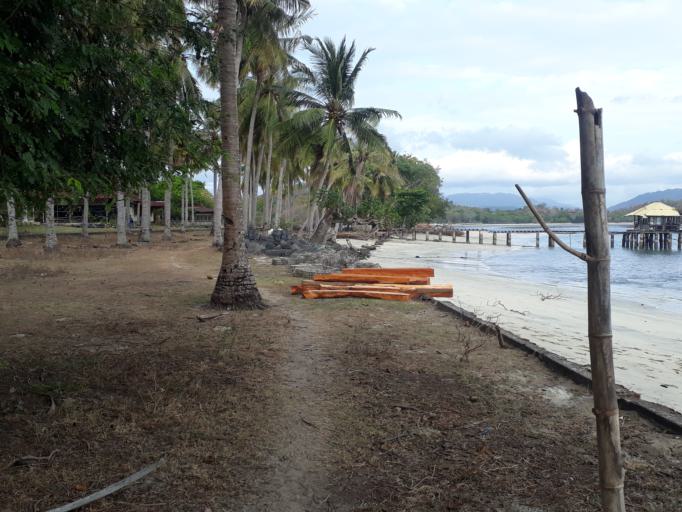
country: ID
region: West Nusa Tenggara
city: Tawun
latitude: -8.7440
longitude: 115.8886
